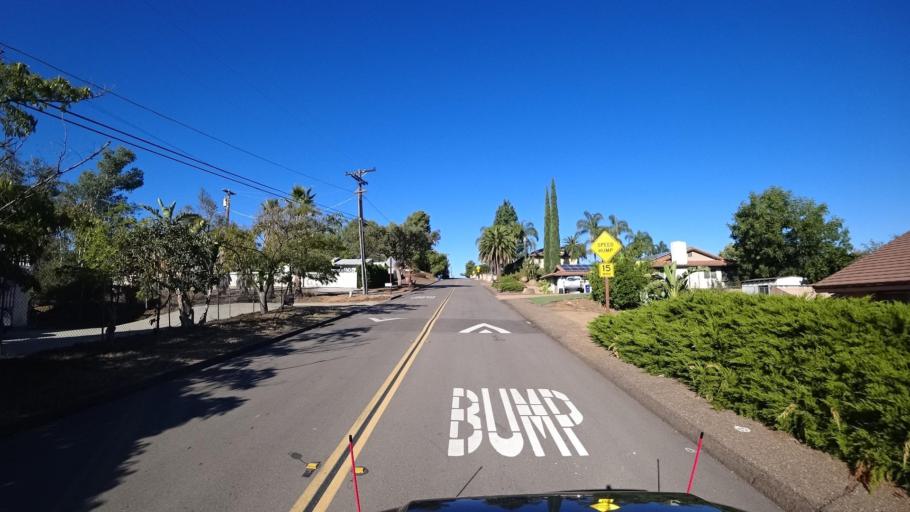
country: US
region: California
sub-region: San Diego County
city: Alpine
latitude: 32.8297
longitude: -116.7557
